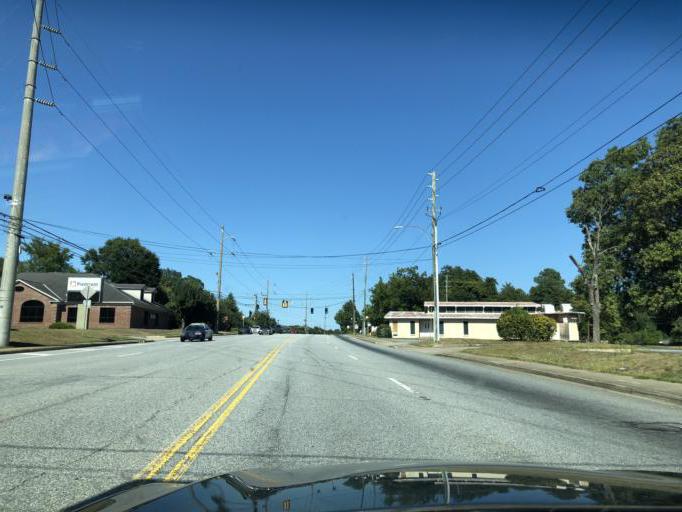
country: US
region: Georgia
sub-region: Muscogee County
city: Columbus
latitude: 32.5028
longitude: -84.9524
